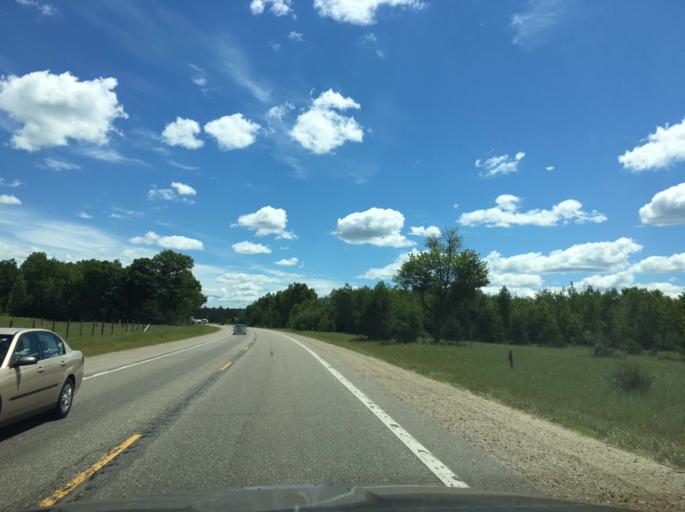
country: US
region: Michigan
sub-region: Osceola County
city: Reed City
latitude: 43.8726
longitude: -85.3959
